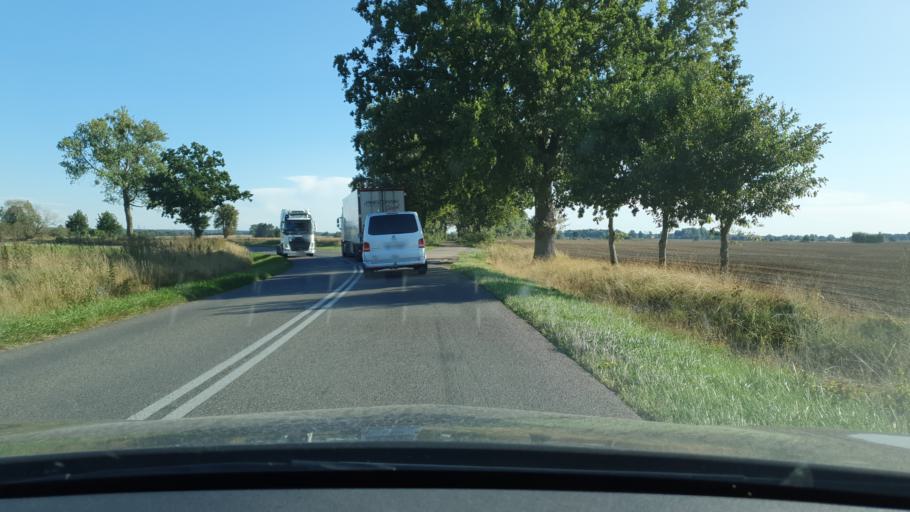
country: PL
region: West Pomeranian Voivodeship
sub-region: Powiat kamienski
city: Golczewo
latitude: 53.8255
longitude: 14.9302
